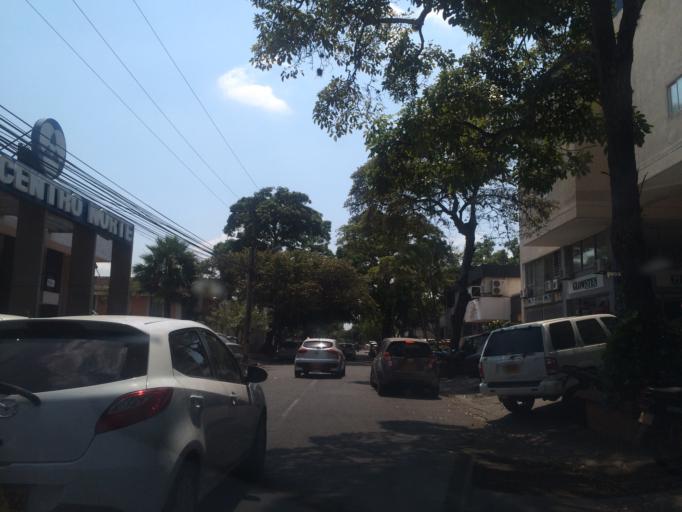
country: CO
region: Valle del Cauca
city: Cali
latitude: 3.4676
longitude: -76.5278
